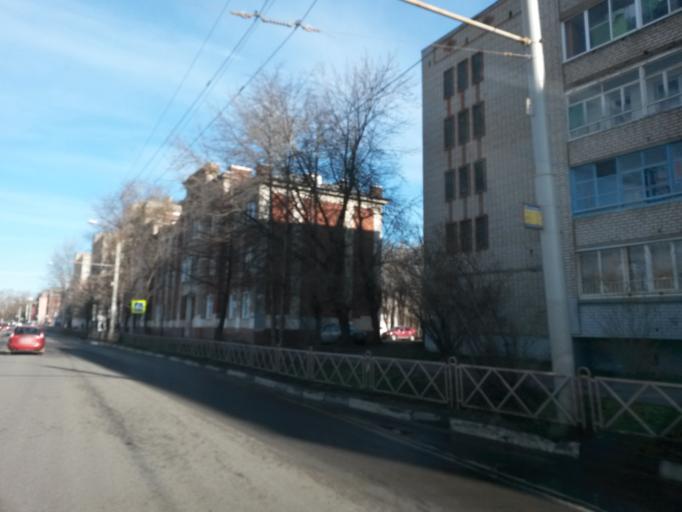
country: RU
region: Jaroslavl
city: Yaroslavl
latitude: 57.6232
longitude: 39.8428
